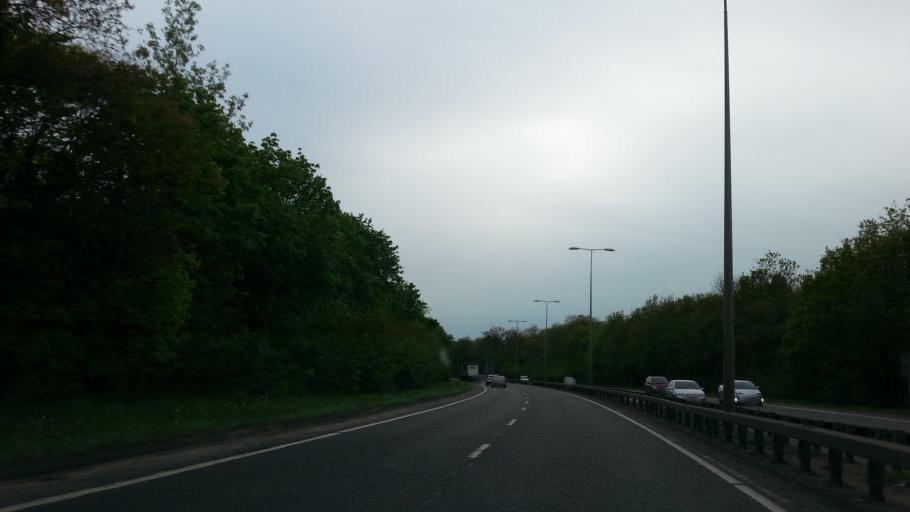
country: GB
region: England
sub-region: Peterborough
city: Marholm
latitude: 52.5943
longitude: -0.2769
